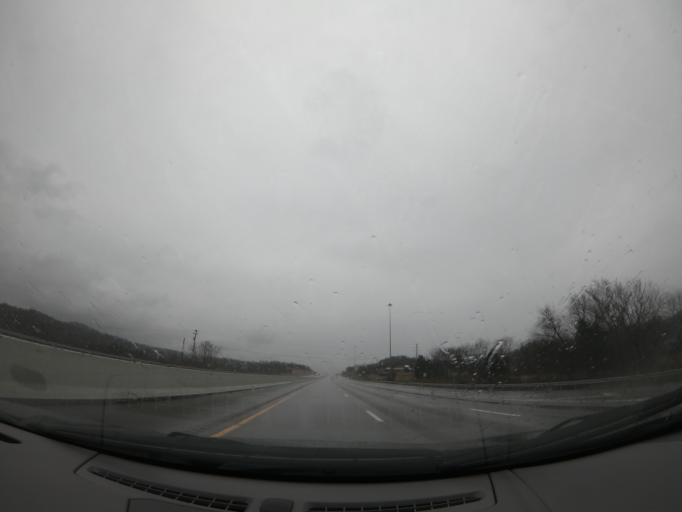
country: US
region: Kentucky
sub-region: Hart County
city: Munfordville
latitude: 37.2348
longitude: -85.9294
